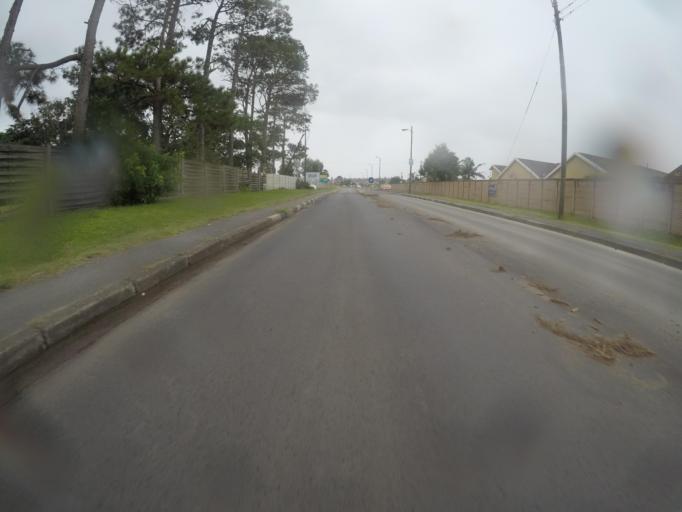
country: ZA
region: Eastern Cape
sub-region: Buffalo City Metropolitan Municipality
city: East London
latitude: -32.9484
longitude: 27.9965
